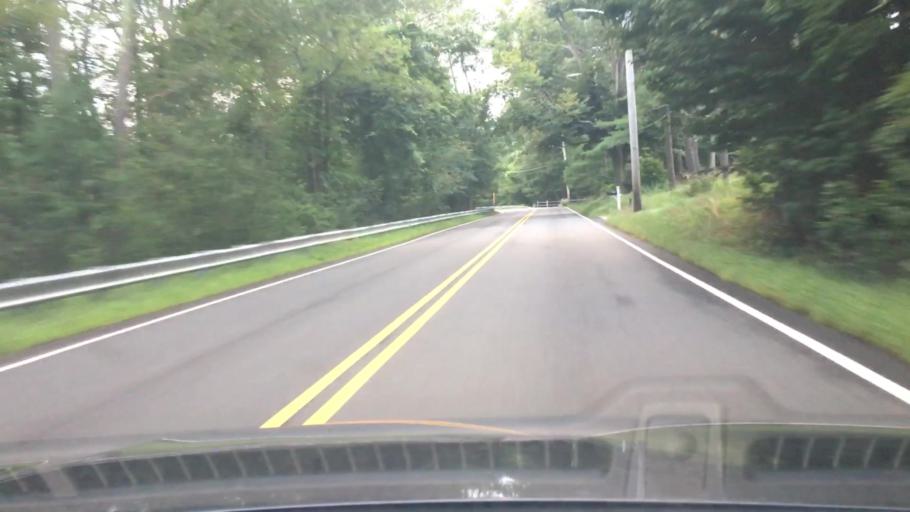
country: US
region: Massachusetts
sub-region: Essex County
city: Middleton
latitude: 42.6216
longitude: -70.9865
